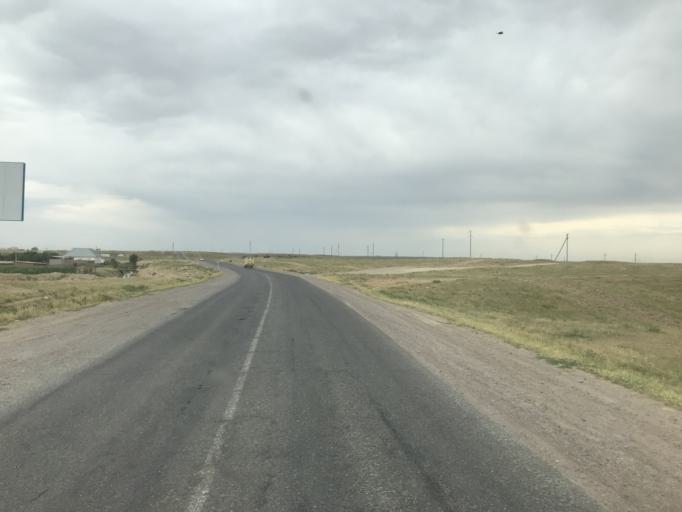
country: UZ
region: Toshkent
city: Yangiyul
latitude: 41.2965
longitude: 68.8477
